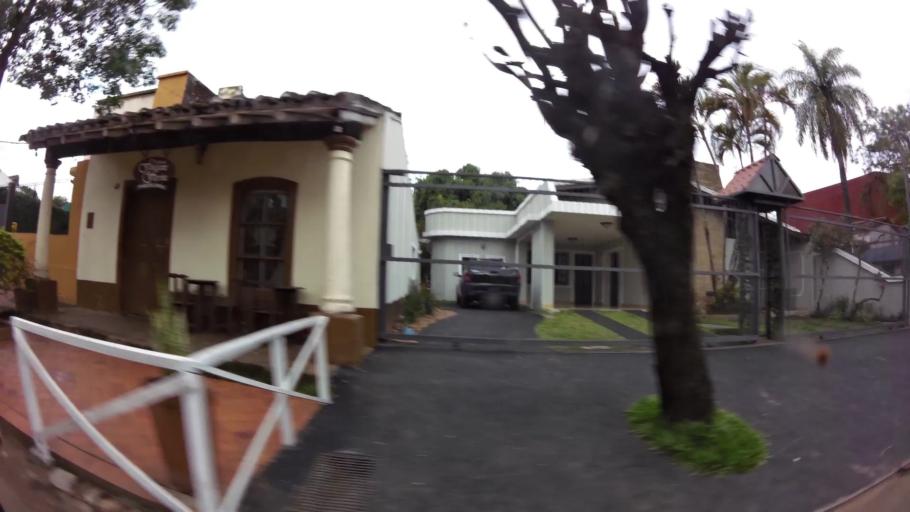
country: PY
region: Central
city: San Lorenzo
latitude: -25.2659
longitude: -57.4960
